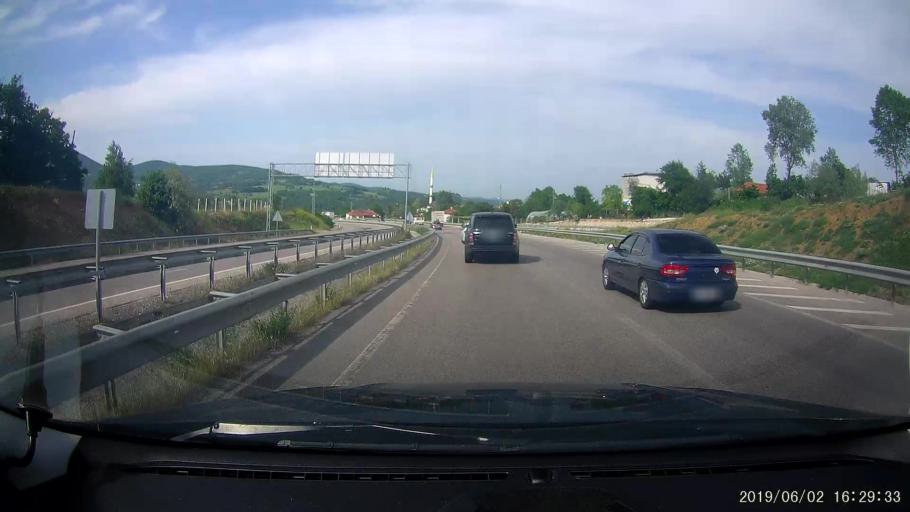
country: TR
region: Samsun
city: Ladik
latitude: 41.0141
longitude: 35.8706
